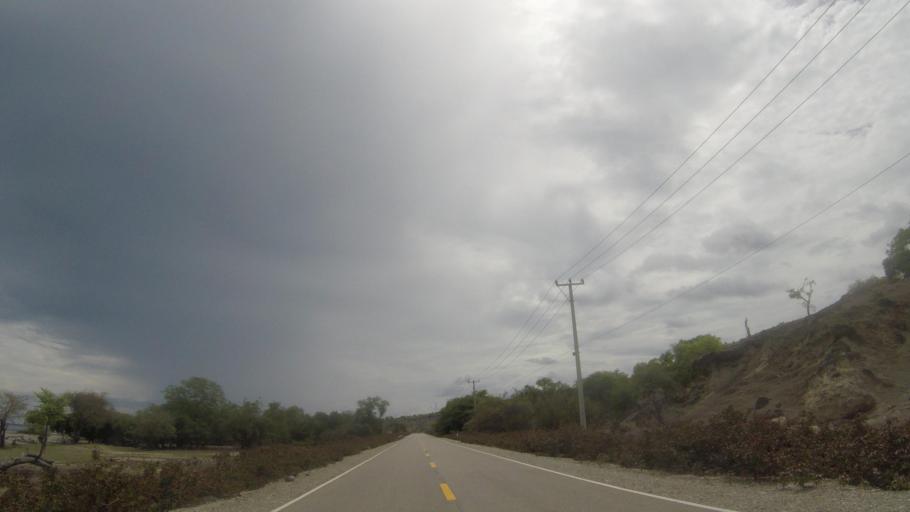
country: TL
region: Baucau
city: Baucau
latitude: -8.4378
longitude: 126.6620
